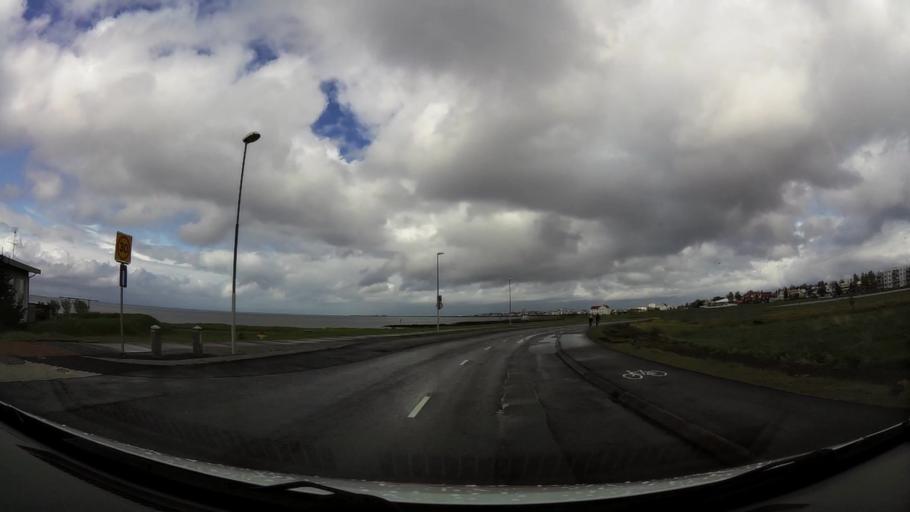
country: IS
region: Capital Region
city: Seltjarnarnes
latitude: 64.1317
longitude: -21.9578
